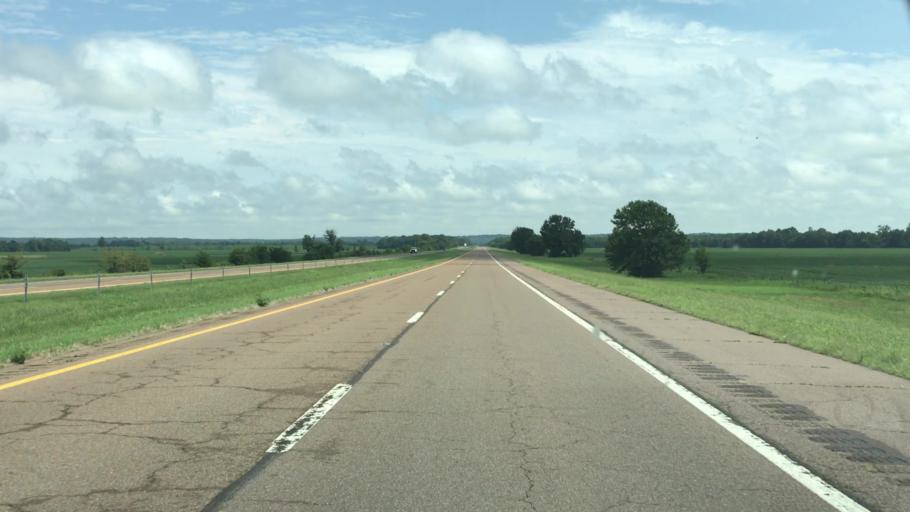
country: US
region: Missouri
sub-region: Pemiscot County
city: Caruthersville
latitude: 36.0882
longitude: -89.5637
